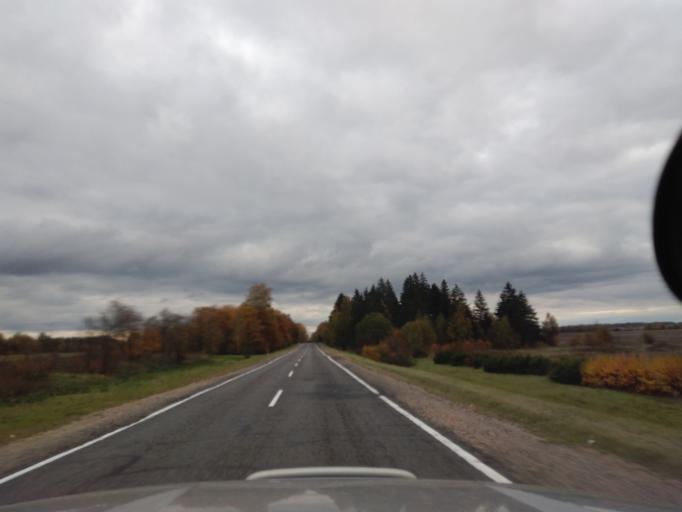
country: BY
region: Minsk
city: Slutsk
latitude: 53.2206
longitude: 27.5118
